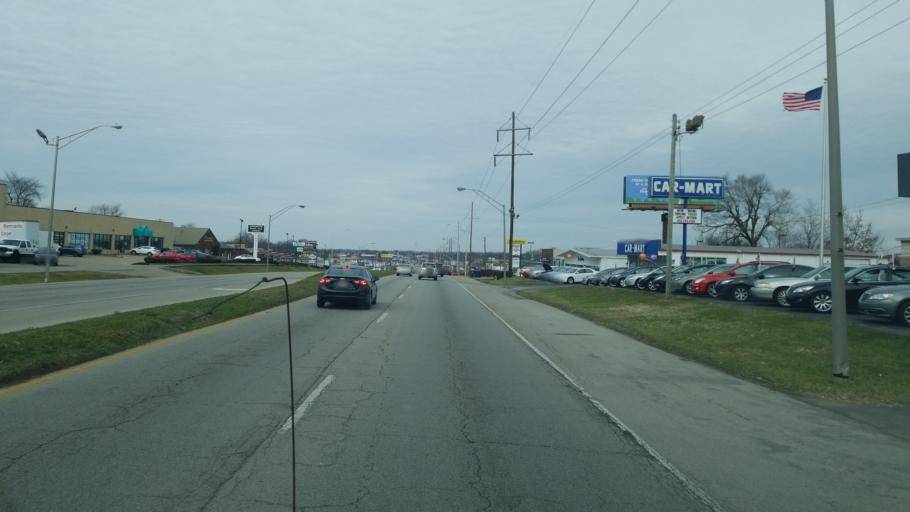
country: US
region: Kentucky
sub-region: Fayette County
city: Lexington-Fayette
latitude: 38.0571
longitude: -84.4619
